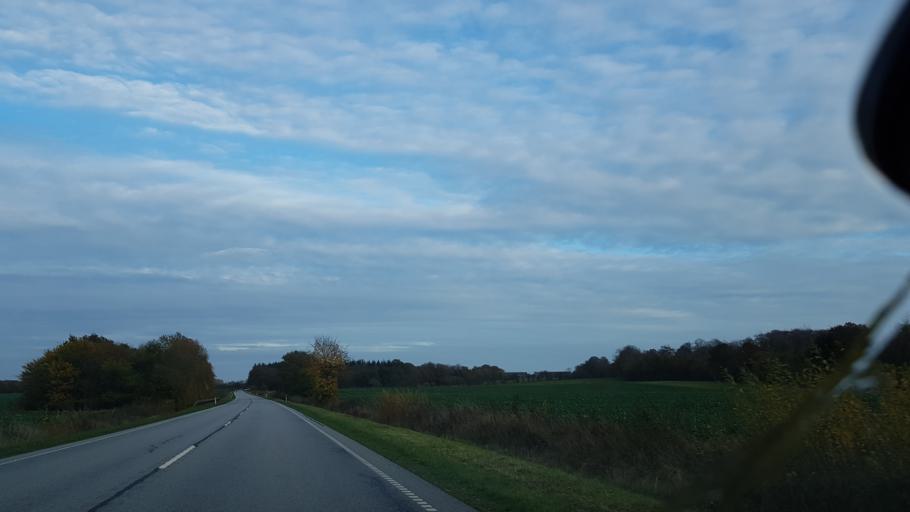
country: DK
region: South Denmark
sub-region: Haderslev Kommune
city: Haderslev
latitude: 55.2940
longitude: 9.4033
